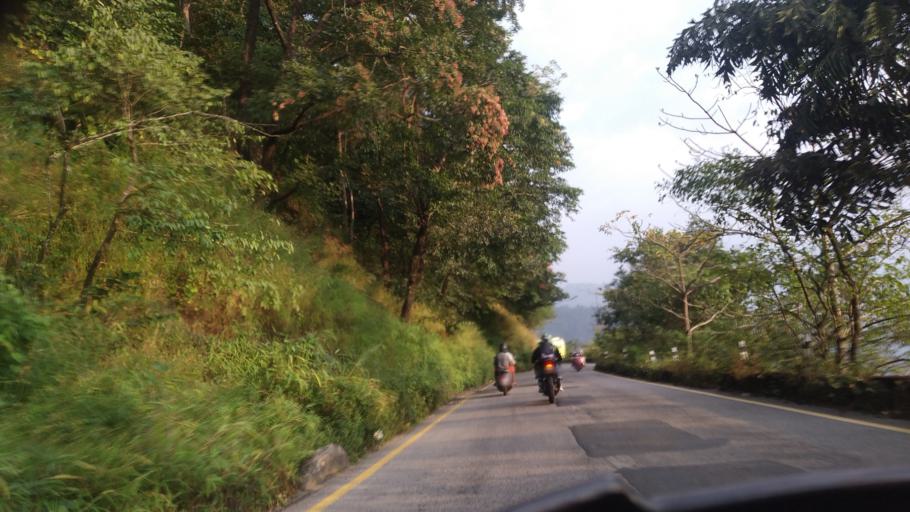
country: IN
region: Kerala
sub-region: Wayanad
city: Kalpetta
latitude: 11.5109
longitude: 76.0172
